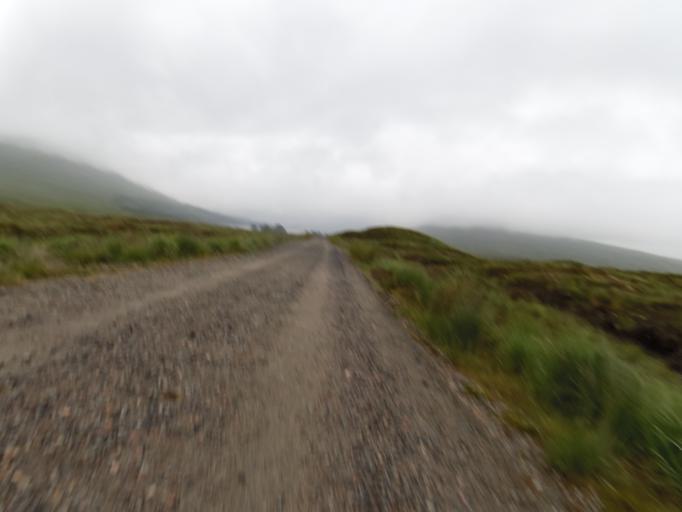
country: GB
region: Scotland
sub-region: Highland
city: Spean Bridge
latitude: 56.7630
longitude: -4.6816
